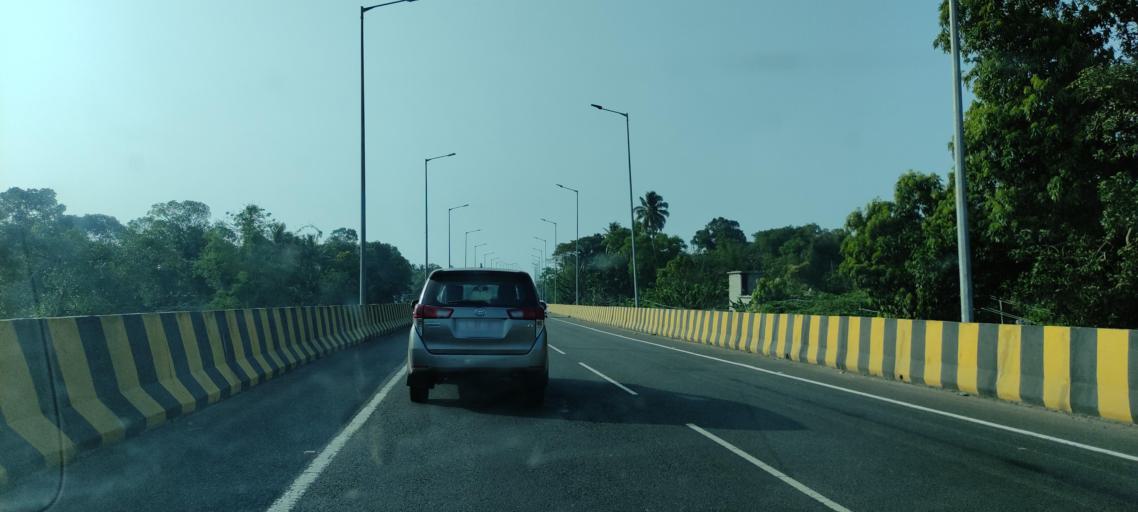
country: IN
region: Kerala
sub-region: Alappuzha
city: Alleppey
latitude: 9.4747
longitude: 76.3287
